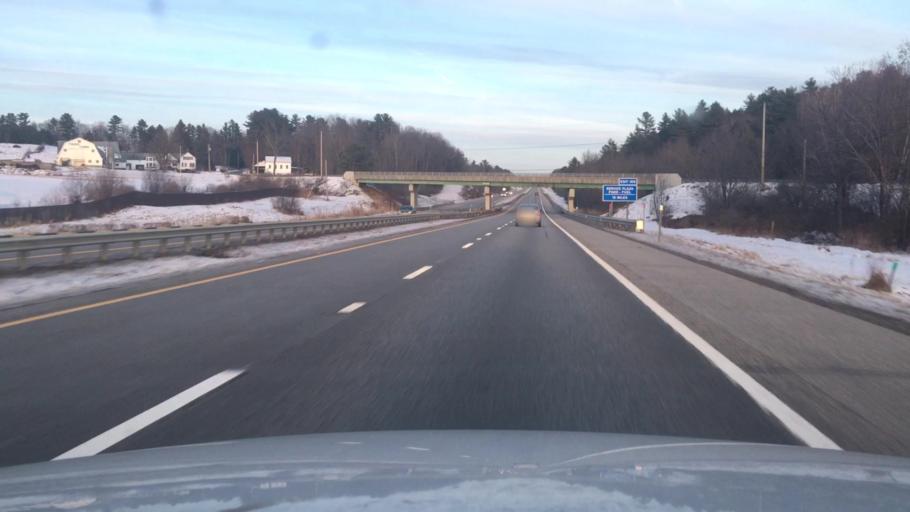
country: US
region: Maine
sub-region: Androscoggin County
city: Sabattus
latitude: 44.1116
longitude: -70.0645
